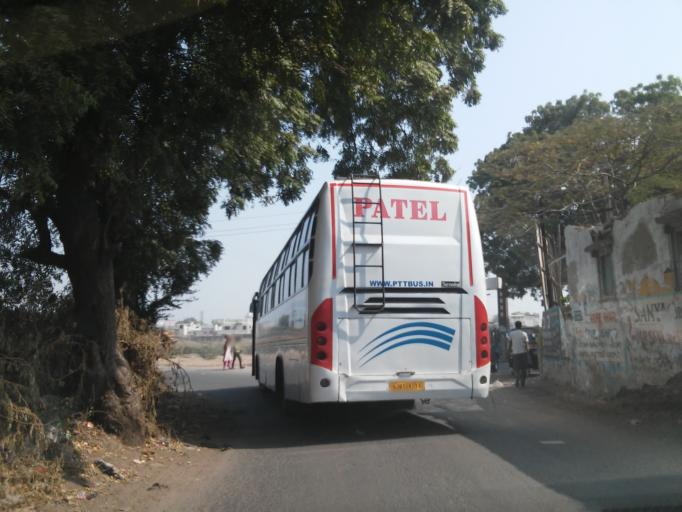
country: IN
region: Gujarat
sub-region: Kachchh
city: Mundra
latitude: 22.8401
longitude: 69.7178
